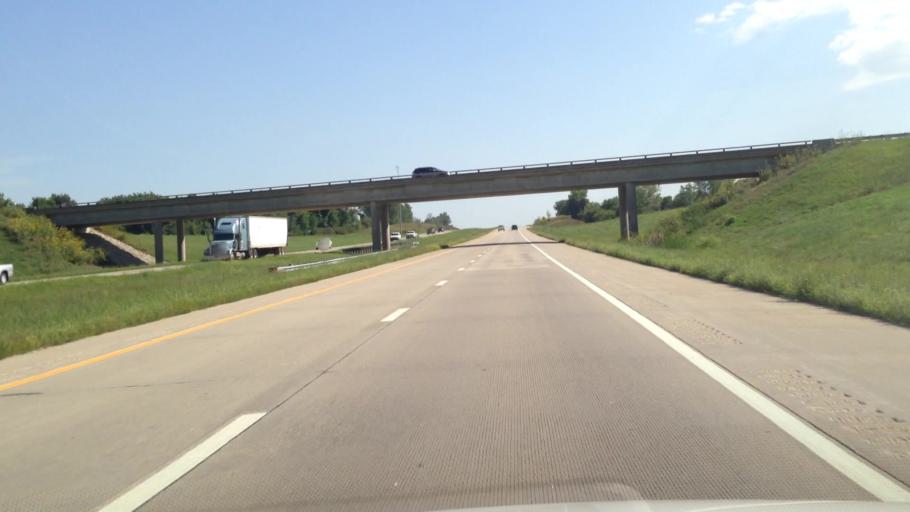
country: US
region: Kansas
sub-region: Miami County
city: Louisburg
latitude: 38.5642
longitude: -94.6942
